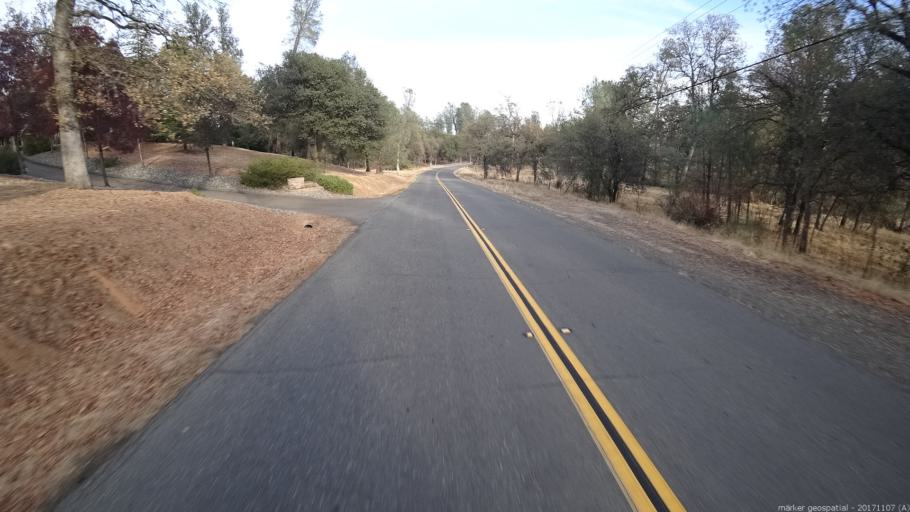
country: US
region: California
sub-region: Shasta County
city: Shasta
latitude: 40.5178
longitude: -122.4730
